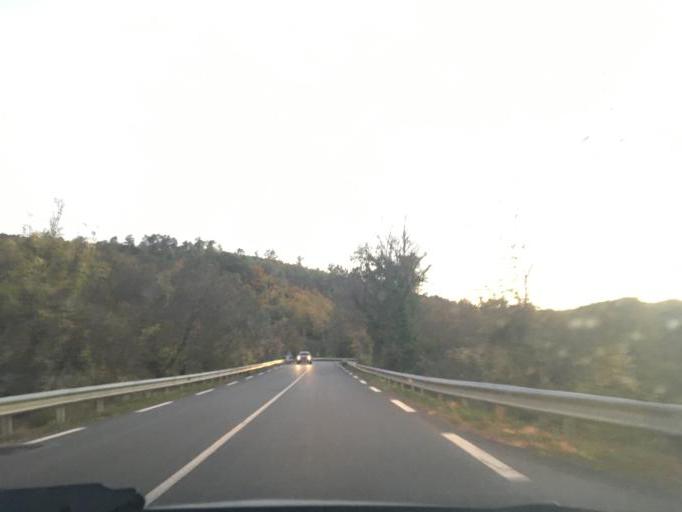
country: FR
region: Provence-Alpes-Cote d'Azur
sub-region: Departement du Var
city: Montferrat
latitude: 43.6040
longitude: 6.4786
